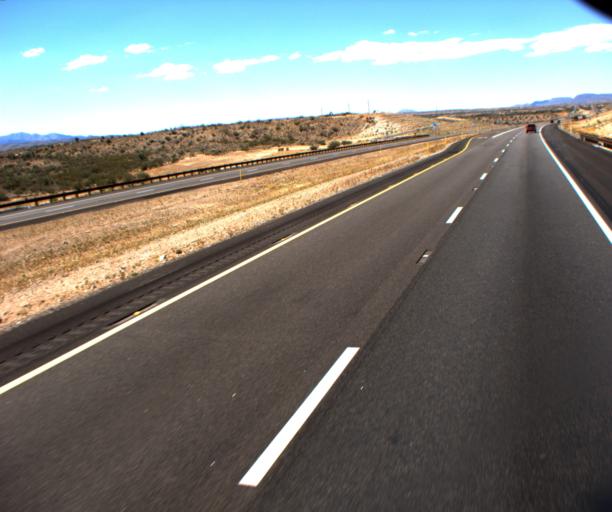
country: US
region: Arizona
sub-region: Mohave County
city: Kingman
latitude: 35.0023
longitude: -113.6641
